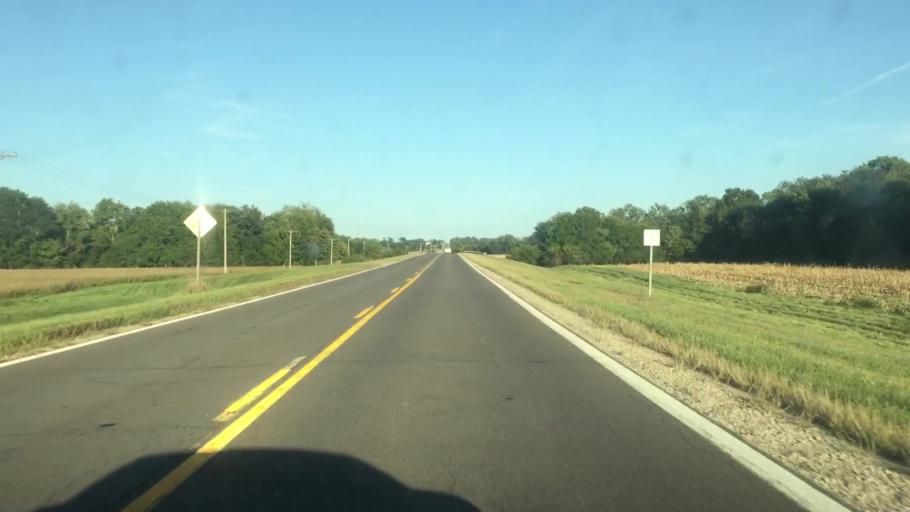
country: US
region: Kansas
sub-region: Brown County
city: Horton
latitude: 39.5507
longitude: -95.5124
